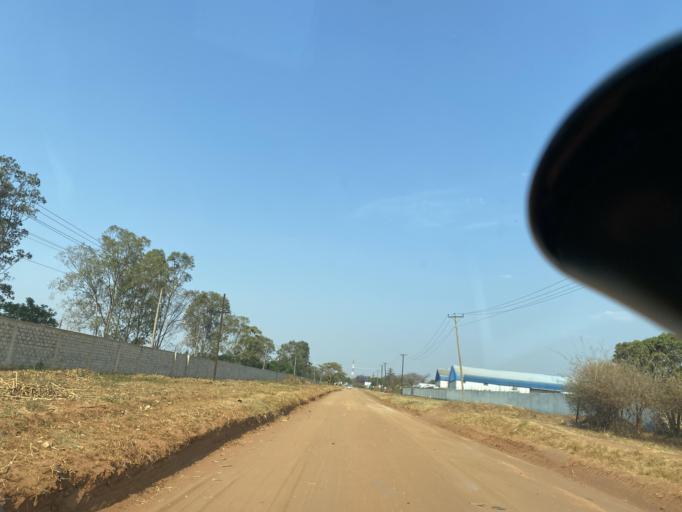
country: ZM
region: Lusaka
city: Lusaka
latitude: -15.4818
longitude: 28.1733
